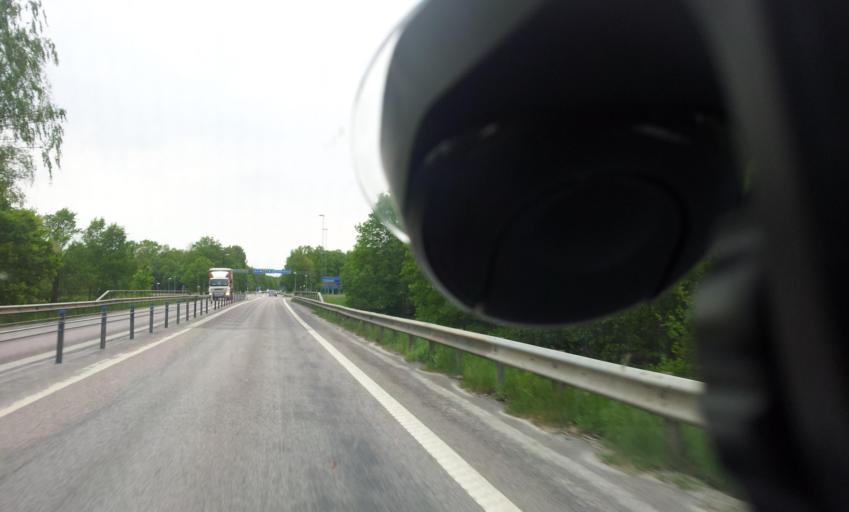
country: SE
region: Kalmar
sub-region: Monsteras Kommun
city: Timmernabben
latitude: 56.9555
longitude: 16.3905
